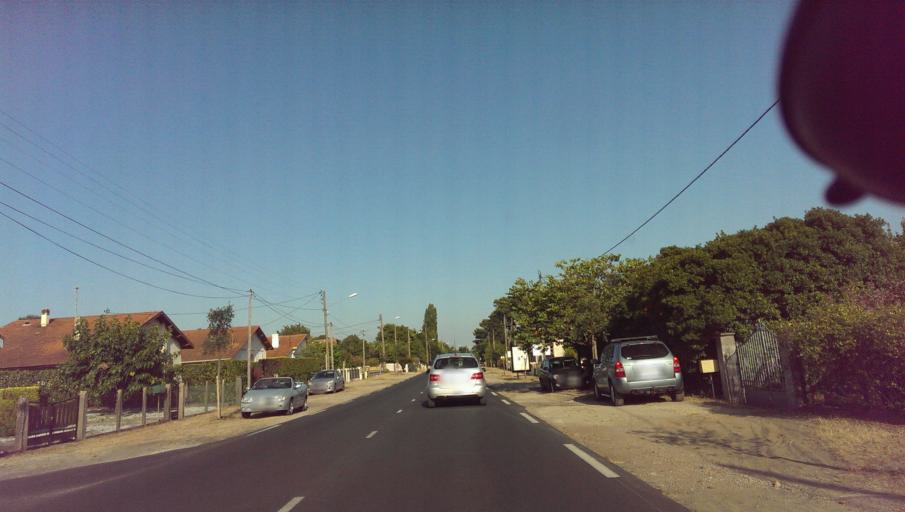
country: FR
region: Aquitaine
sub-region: Departement des Landes
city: Mimizan
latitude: 44.2108
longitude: -1.2569
